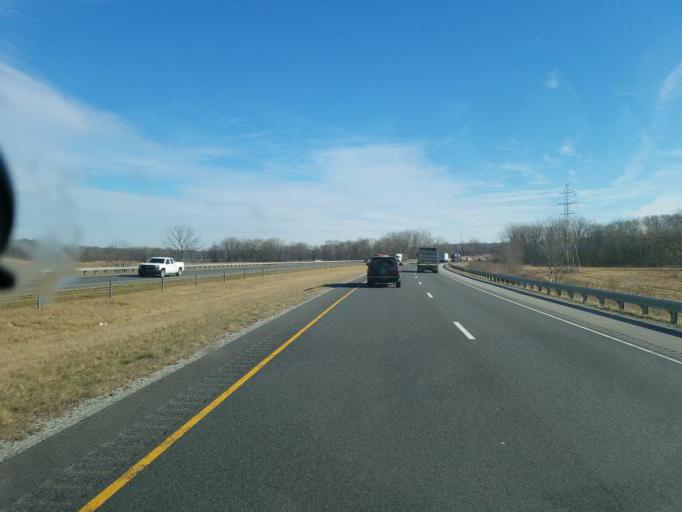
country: US
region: Indiana
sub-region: Henry County
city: Knightstown
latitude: 39.8524
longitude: -85.4833
